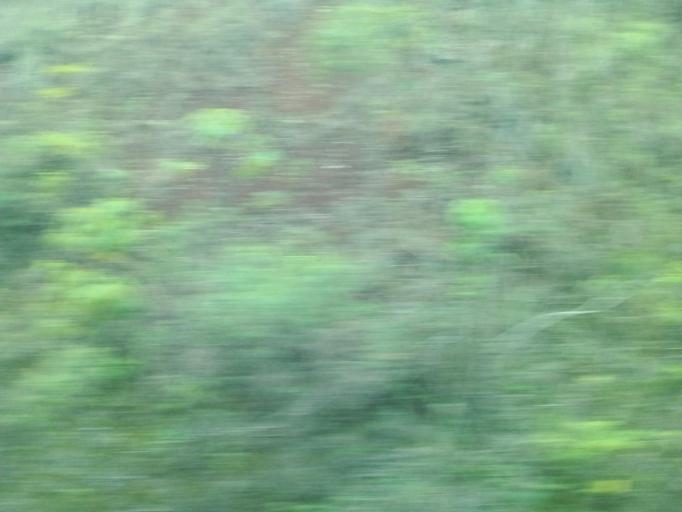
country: BR
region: Minas Gerais
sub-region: Rio Piracicaba
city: Rio Piracicaba
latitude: -19.9728
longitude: -43.2204
